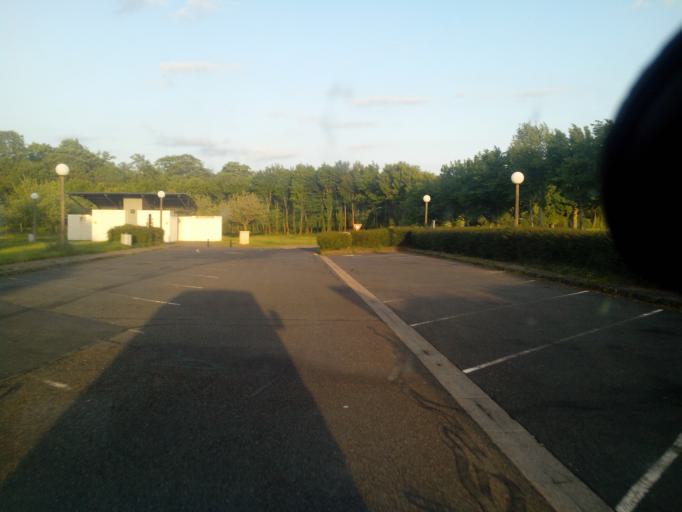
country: FR
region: Picardie
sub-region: Departement de la Somme
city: Oisemont
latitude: 50.0439
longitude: 1.7618
